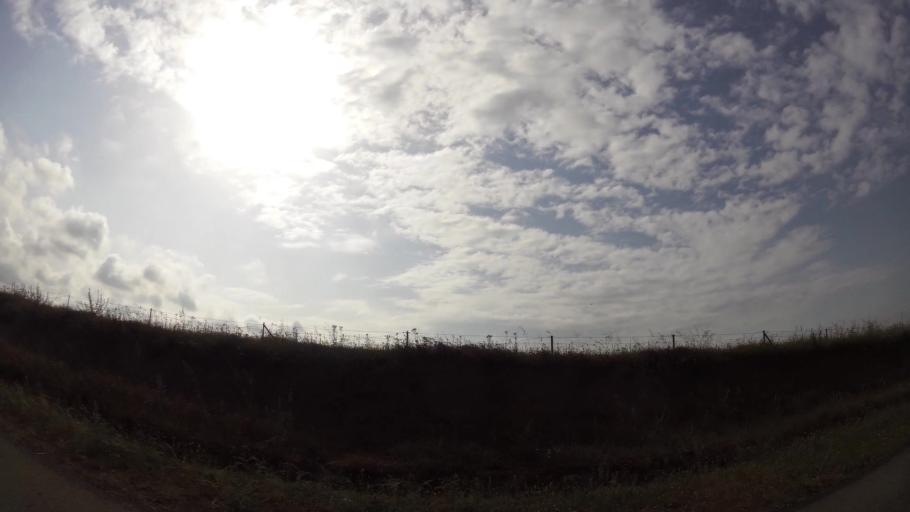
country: MA
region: Rabat-Sale-Zemmour-Zaer
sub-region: Khemisset
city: Tiflet
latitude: 33.8787
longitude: -6.3239
